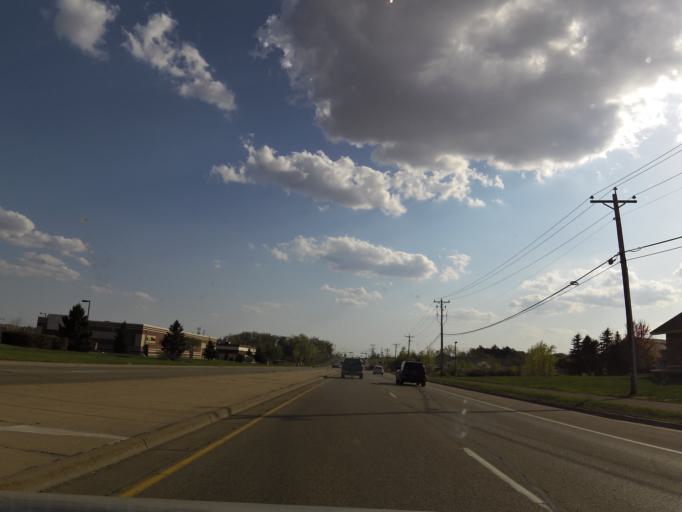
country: US
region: Minnesota
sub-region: Washington County
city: Stillwater
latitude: 45.0417
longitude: -92.8410
